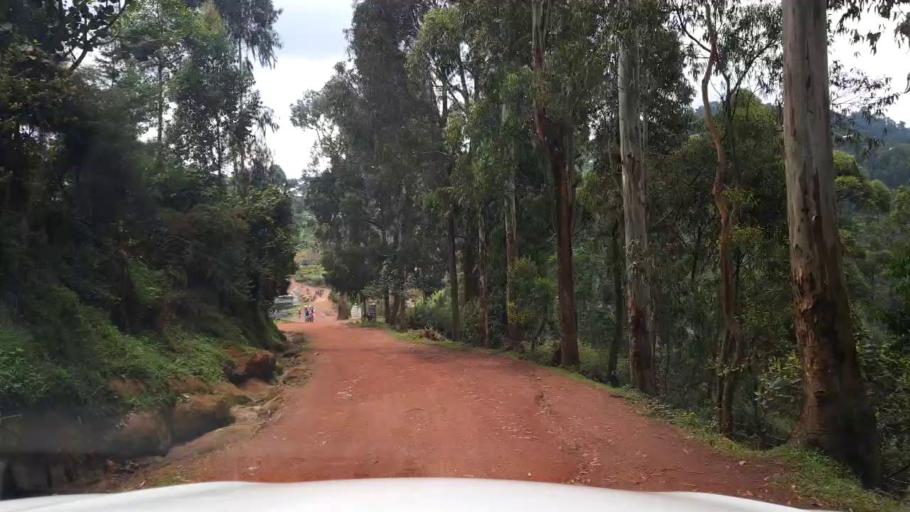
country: UG
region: Western Region
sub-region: Kisoro District
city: Kisoro
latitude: -1.4198
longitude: 29.8318
